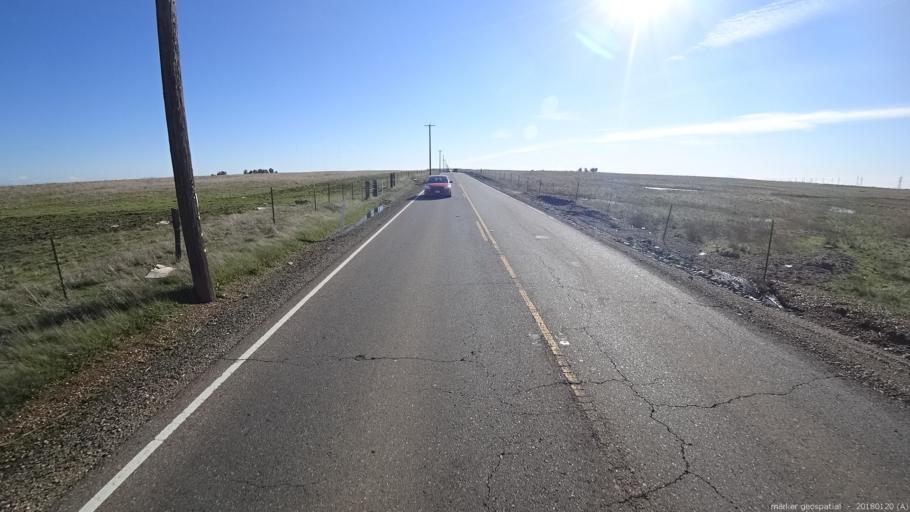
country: US
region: California
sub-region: Sacramento County
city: Gold River
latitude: 38.5679
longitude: -121.1873
